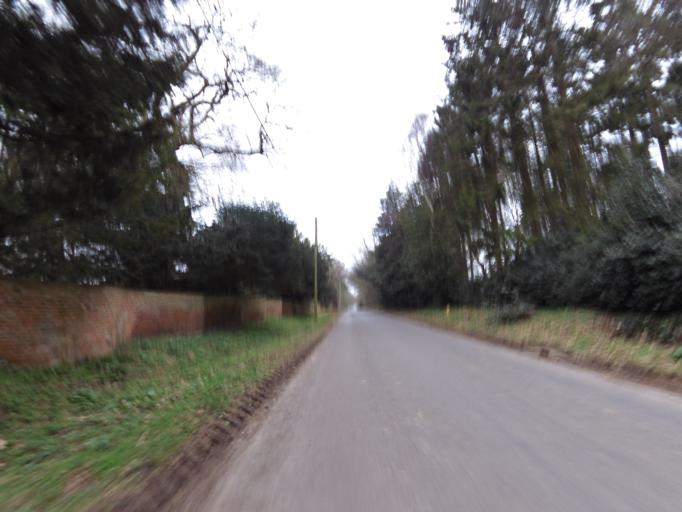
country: GB
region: England
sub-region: Suffolk
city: Framlingham
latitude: 52.1845
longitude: 1.3347
